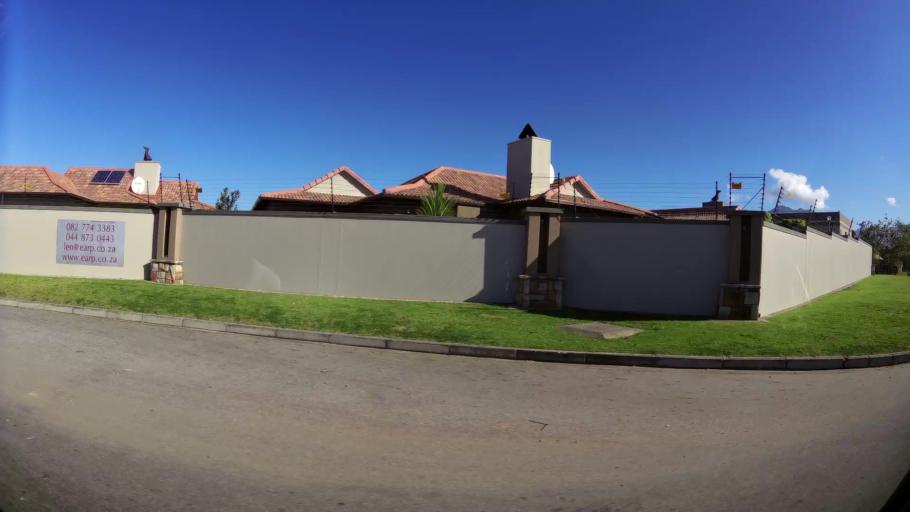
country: ZA
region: Western Cape
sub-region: Eden District Municipality
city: George
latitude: -33.9612
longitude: 22.4246
